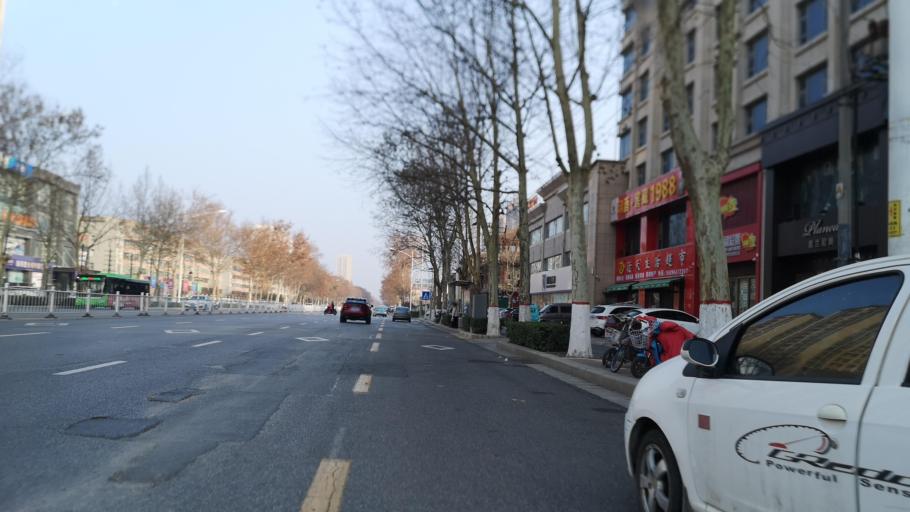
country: CN
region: Henan Sheng
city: Zhongyuanlu
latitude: 35.7796
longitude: 115.0503
